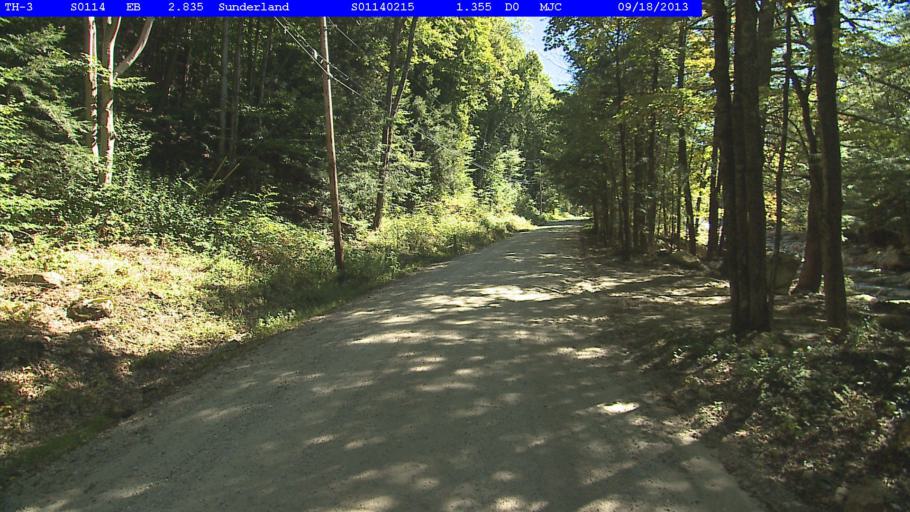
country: US
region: Vermont
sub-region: Bennington County
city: Arlington
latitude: 43.0539
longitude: -73.1154
